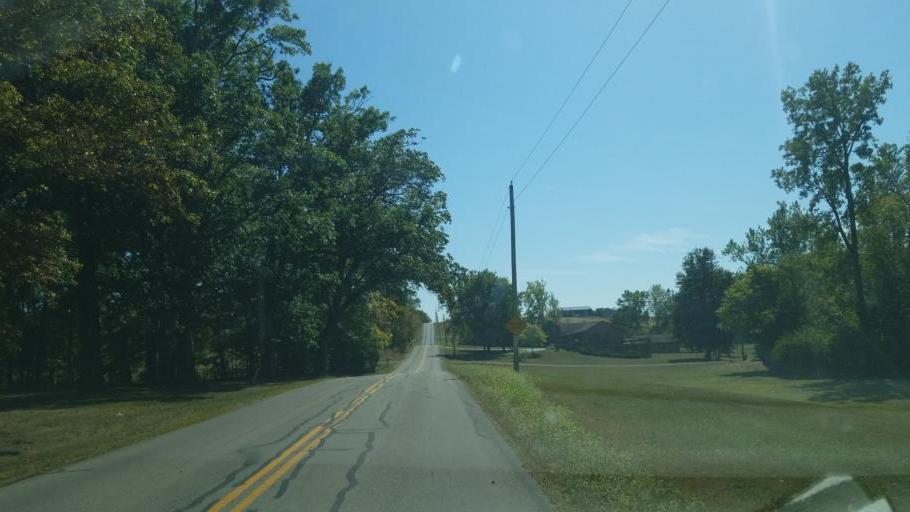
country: US
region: Ohio
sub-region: Logan County
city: Bellefontaine
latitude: 40.4006
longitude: -83.7692
